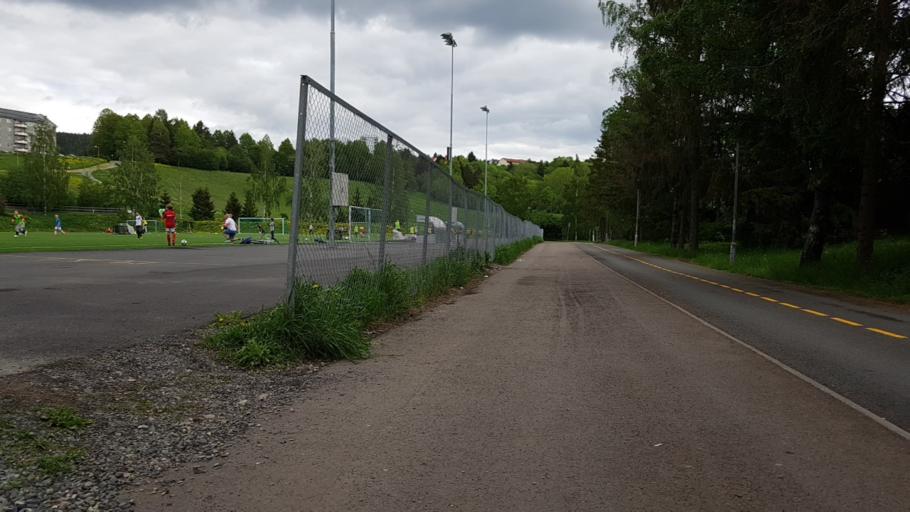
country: NO
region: Oslo
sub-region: Oslo
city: Oslo
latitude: 59.9441
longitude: 10.8157
